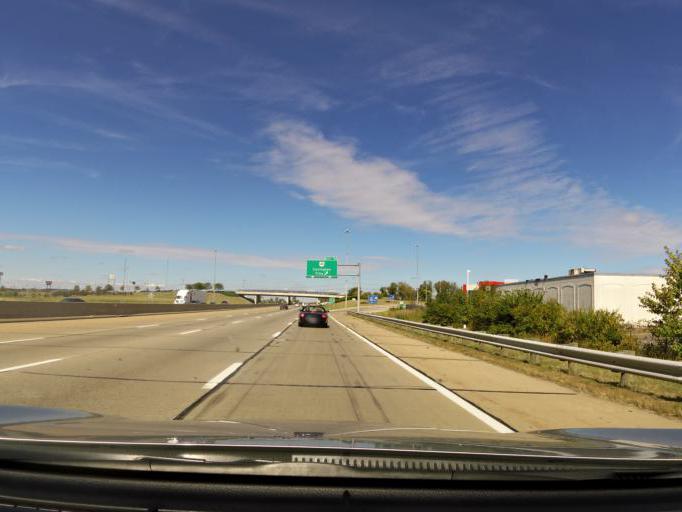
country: US
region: Ohio
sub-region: Miami County
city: Troy
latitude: 40.0492
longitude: -84.2320
